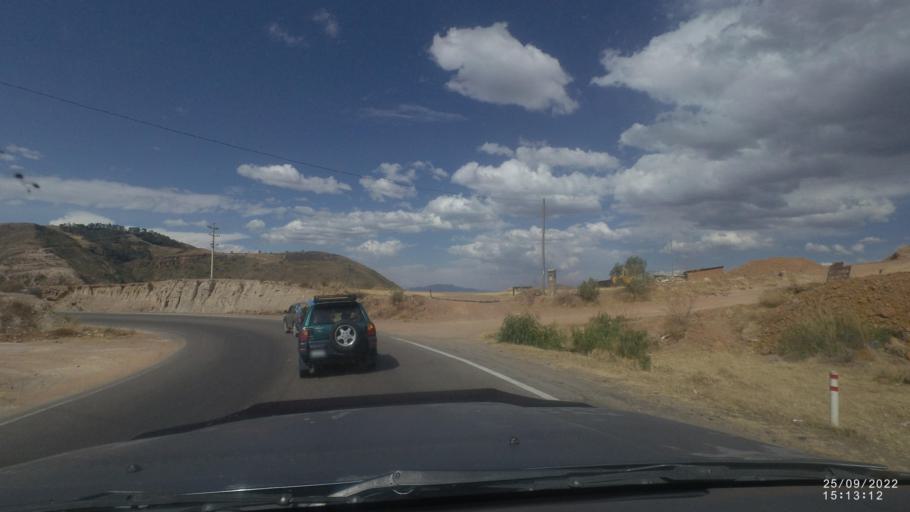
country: BO
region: Cochabamba
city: Irpa Irpa
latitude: -17.6538
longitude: -66.3911
